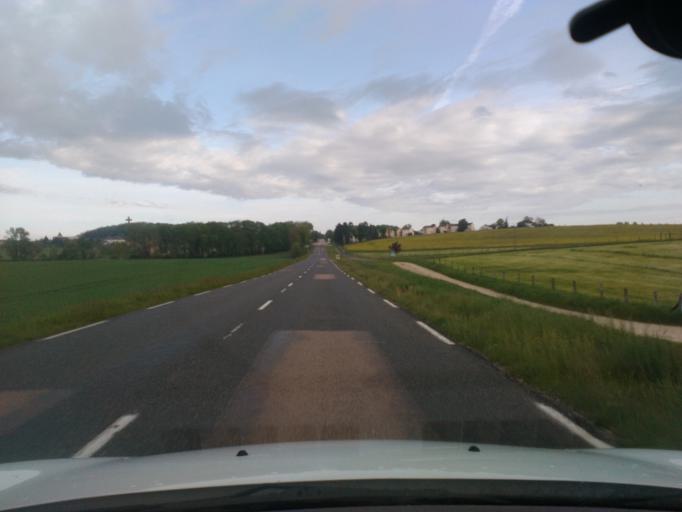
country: FR
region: Champagne-Ardenne
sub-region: Departement de la Haute-Marne
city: Lavilleneuve-au-Roi
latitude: 48.2202
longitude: 4.8994
